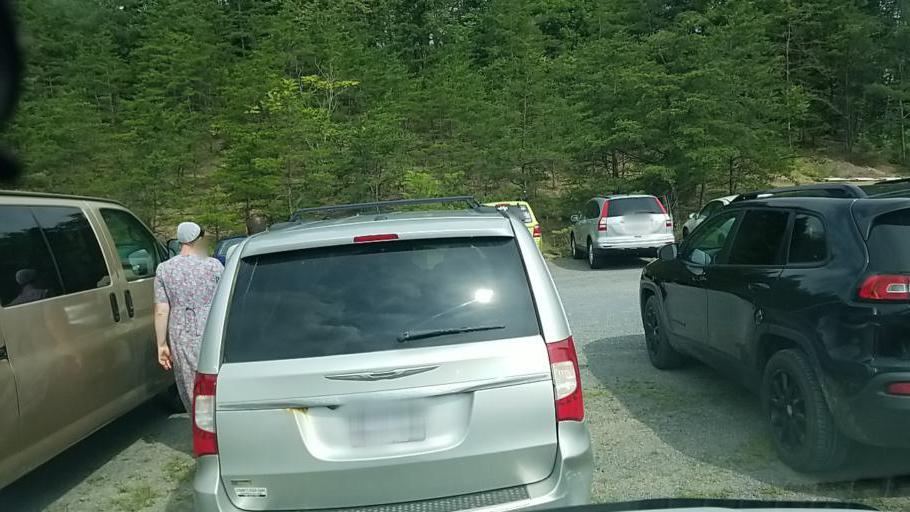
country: US
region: Pennsylvania
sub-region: Dauphin County
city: Matamoras
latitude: 40.5003
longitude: -76.8957
